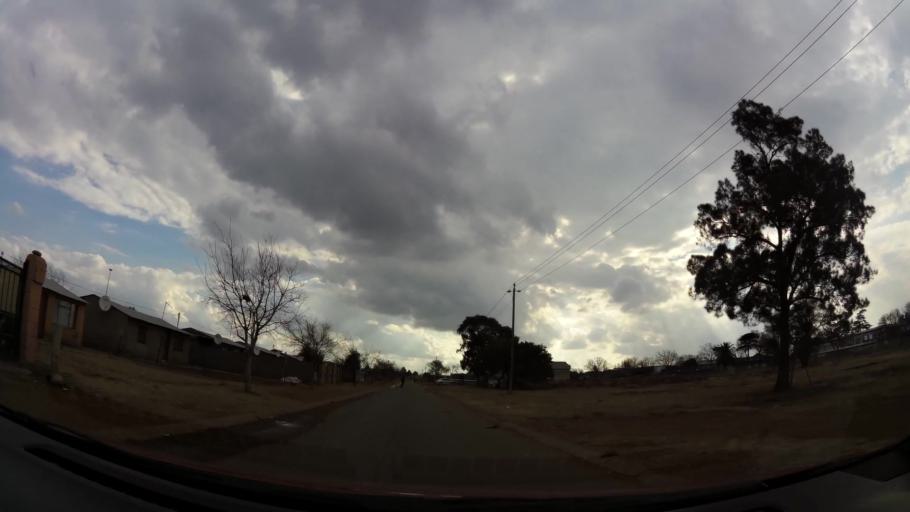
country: ZA
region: Gauteng
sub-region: Sedibeng District Municipality
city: Vanderbijlpark
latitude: -26.6623
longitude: 27.8512
